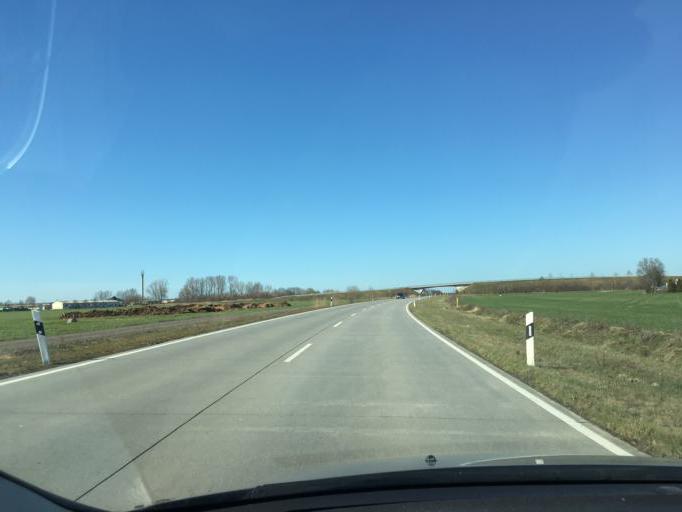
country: DE
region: Saxony
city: Grossposna
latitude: 51.2703
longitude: 12.4541
